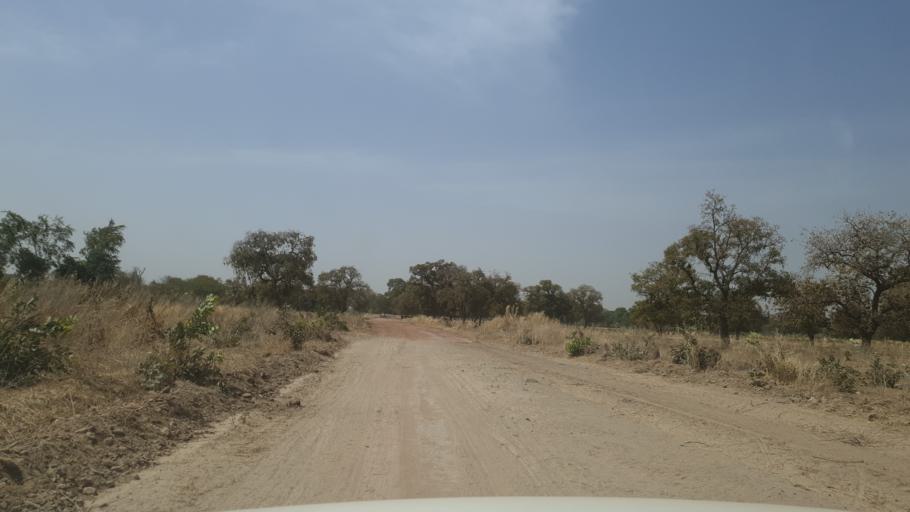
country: ML
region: Koulikoro
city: Kolokani
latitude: 13.4772
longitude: -8.1841
